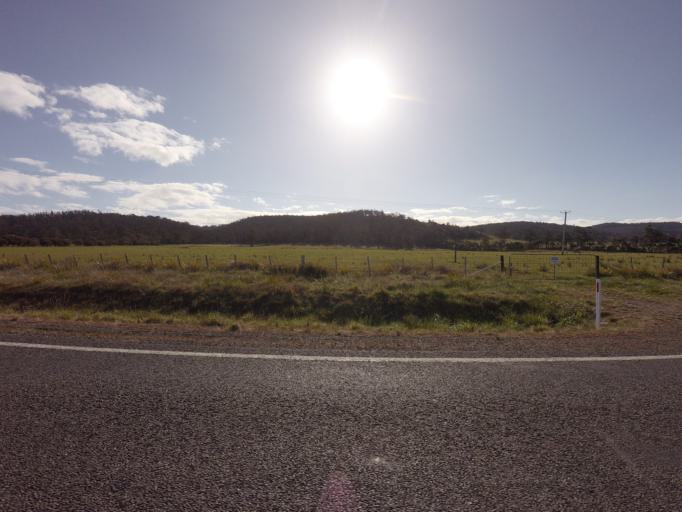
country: AU
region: Tasmania
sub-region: Sorell
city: Sorell
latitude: -42.4584
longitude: 147.9269
